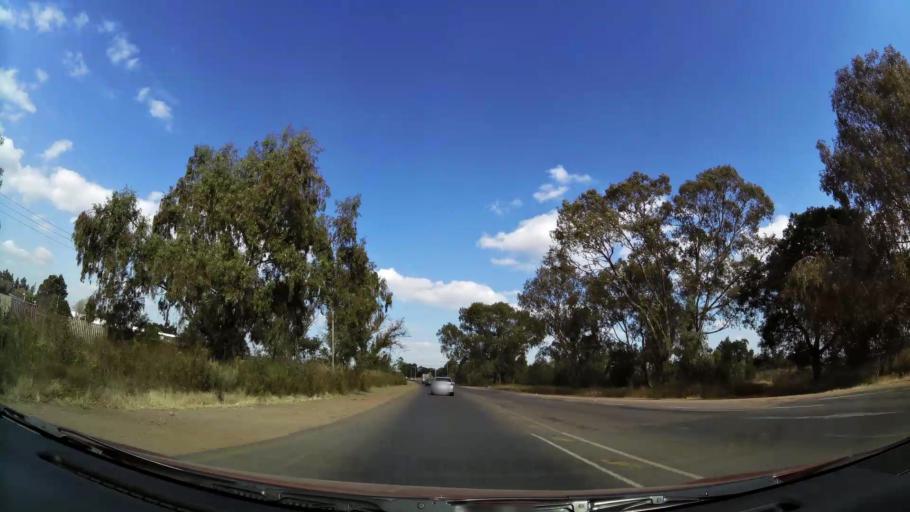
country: ZA
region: Gauteng
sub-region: Ekurhuleni Metropolitan Municipality
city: Tembisa
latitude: -26.0075
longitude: 28.2505
